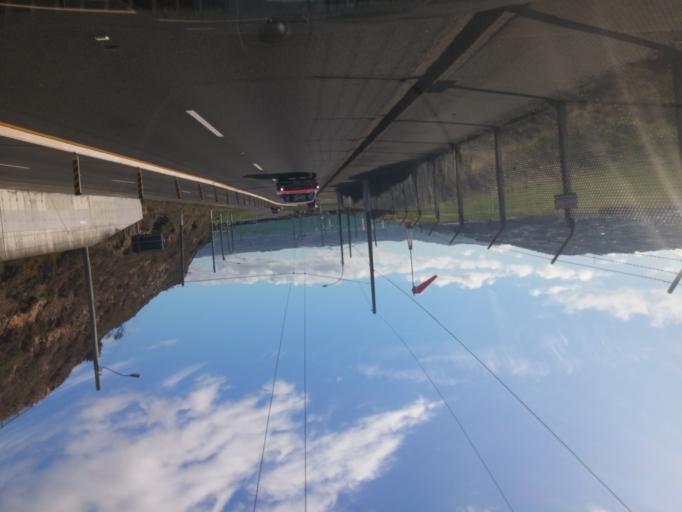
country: NZ
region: Wellington
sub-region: Wellington City
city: Wellington
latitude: -41.3186
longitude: 174.8093
